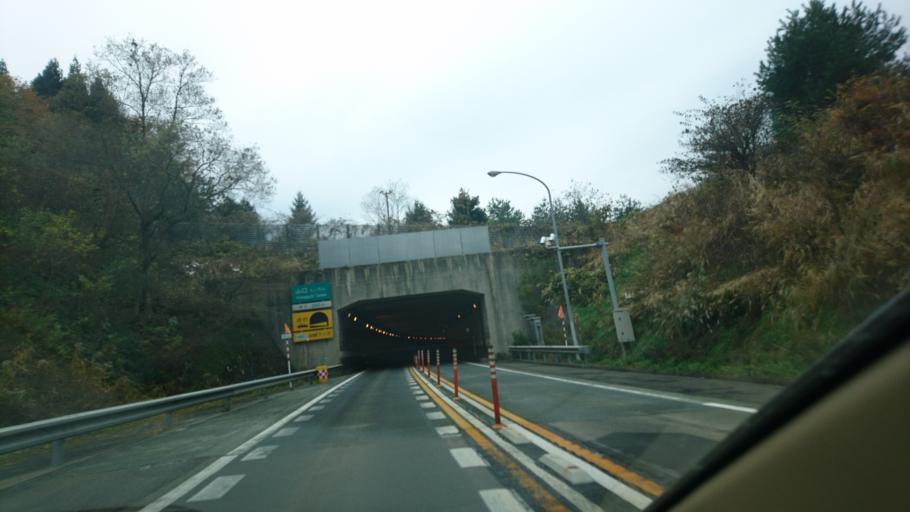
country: JP
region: Iwate
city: Kitakami
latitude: 39.2935
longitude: 140.9722
